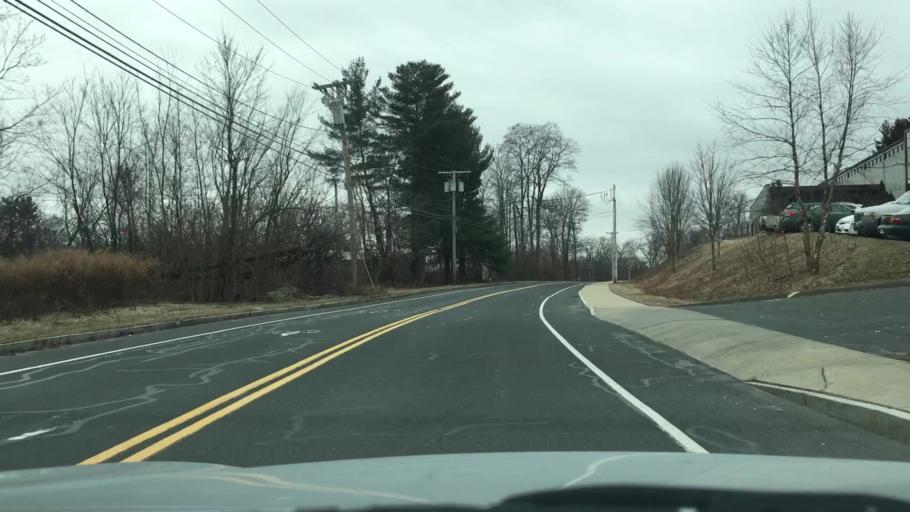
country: US
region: Massachusetts
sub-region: Hampshire County
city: Northampton
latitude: 42.3097
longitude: -72.6439
